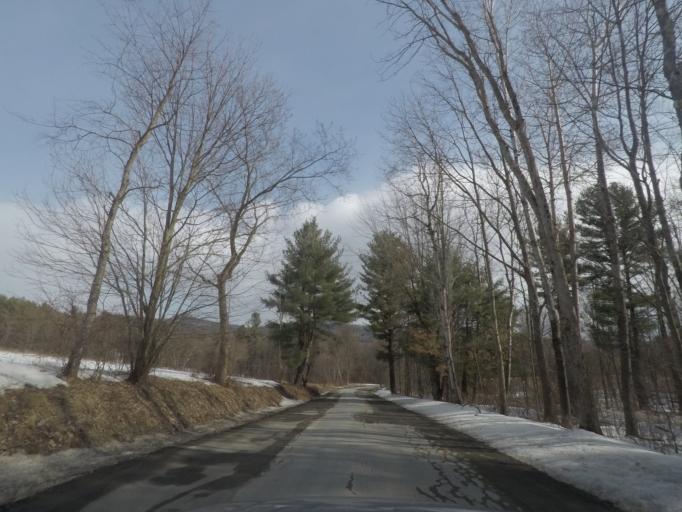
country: US
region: New York
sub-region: Rensselaer County
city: Poestenkill
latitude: 42.7762
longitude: -73.5526
